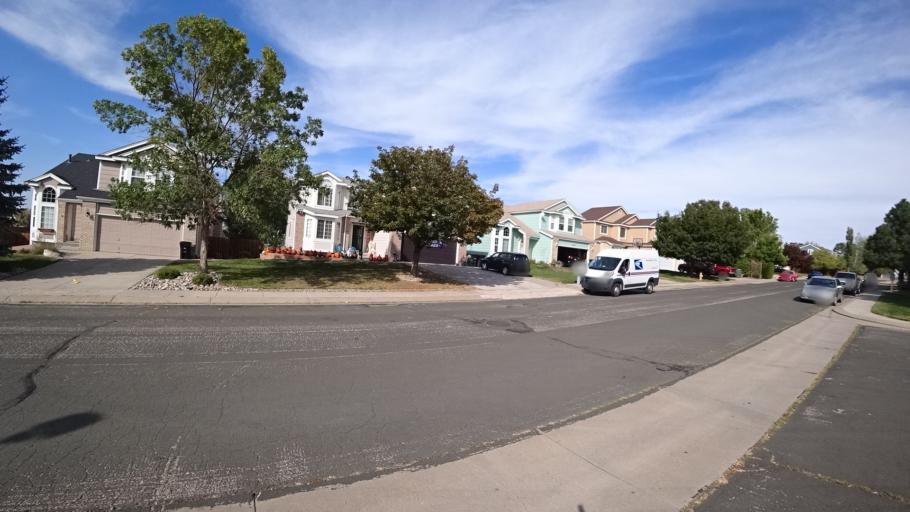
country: US
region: Colorado
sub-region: El Paso County
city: Cimarron Hills
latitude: 38.9041
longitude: -104.6911
